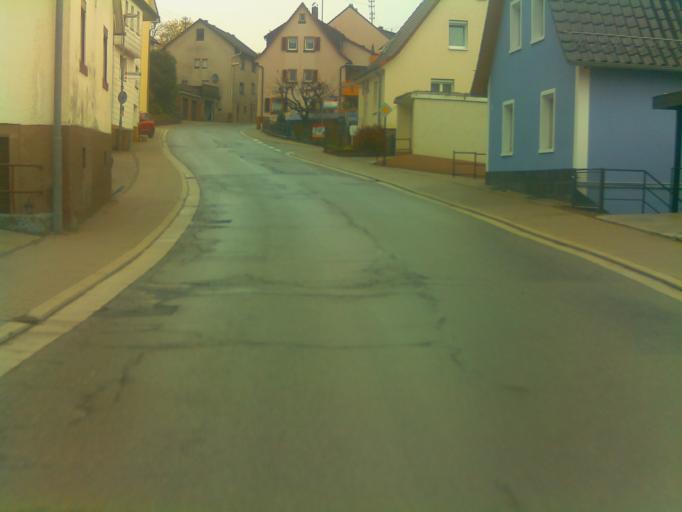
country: DE
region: Baden-Wuerttemberg
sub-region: Karlsruhe Region
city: Wilhelmsfeld
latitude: 49.4662
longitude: 8.7603
